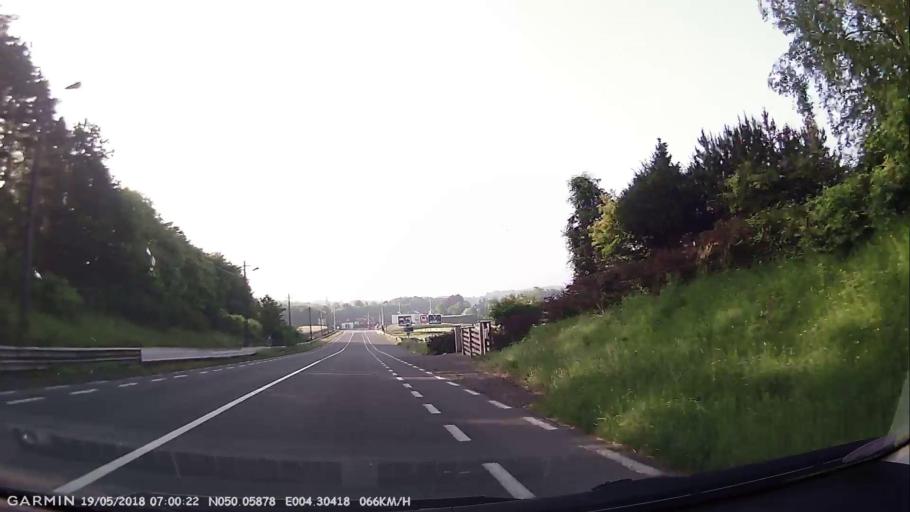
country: BE
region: Wallonia
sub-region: Province du Hainaut
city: Chimay
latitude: 50.0585
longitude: 4.3044
